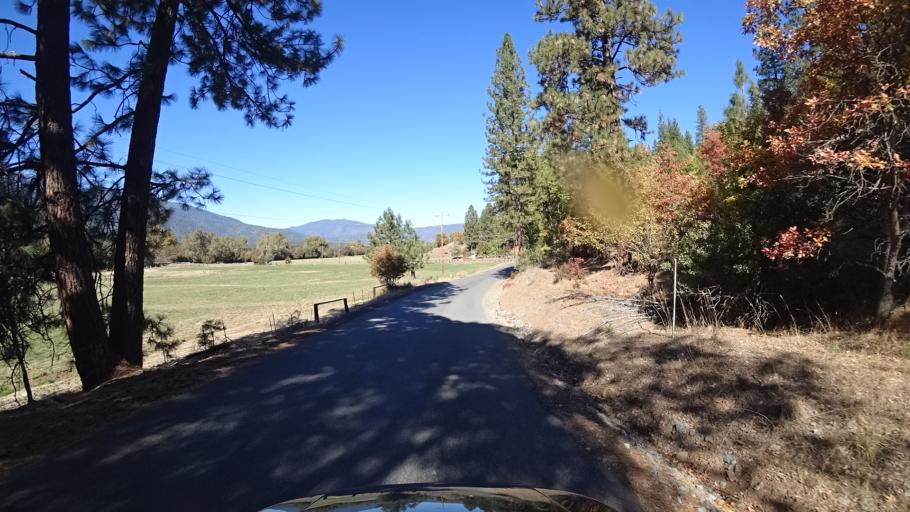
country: US
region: California
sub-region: Siskiyou County
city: Yreka
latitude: 41.5804
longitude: -122.9577
